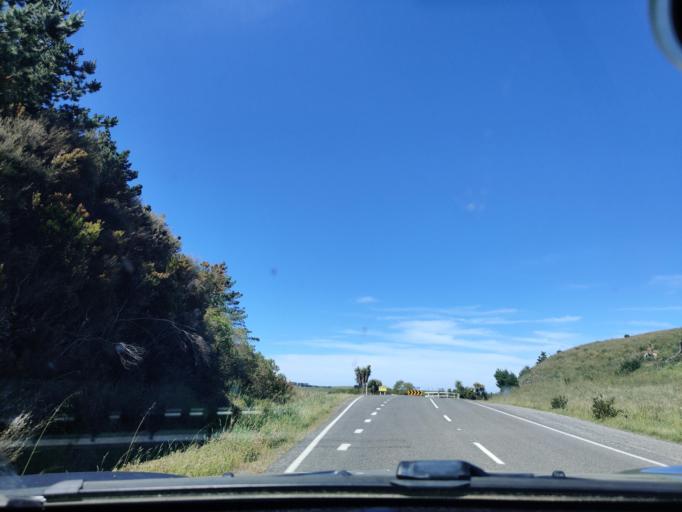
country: NZ
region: Wellington
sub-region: Upper Hutt City
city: Upper Hutt
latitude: -41.3647
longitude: 175.1990
